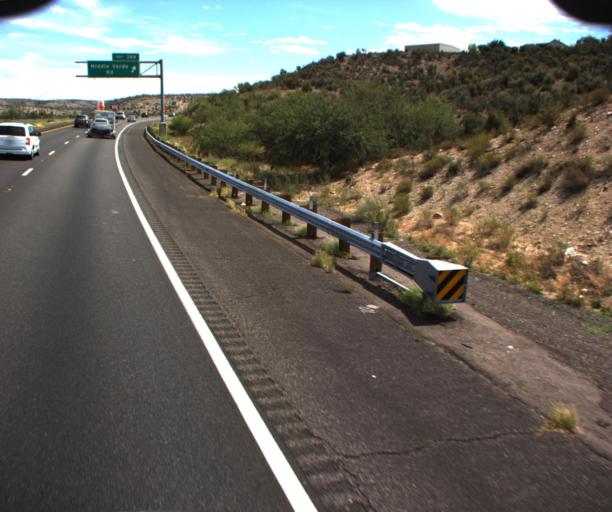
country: US
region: Arizona
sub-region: Yavapai County
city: Camp Verde
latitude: 34.6070
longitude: -111.8686
